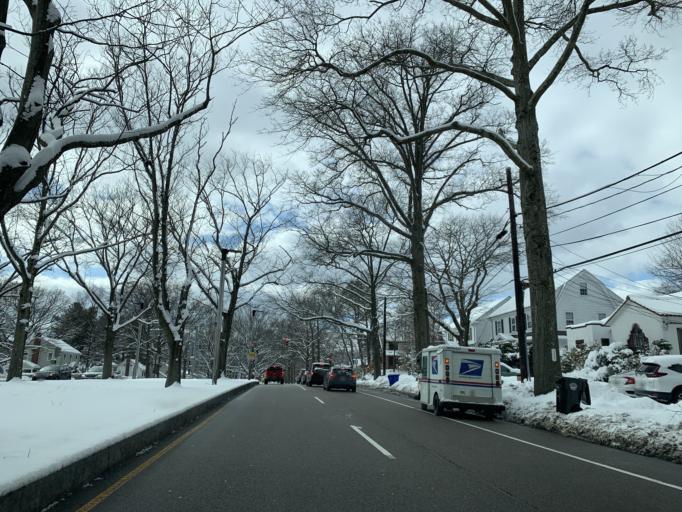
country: US
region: Massachusetts
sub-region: Suffolk County
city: Jamaica Plain
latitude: 42.2964
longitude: -71.1496
